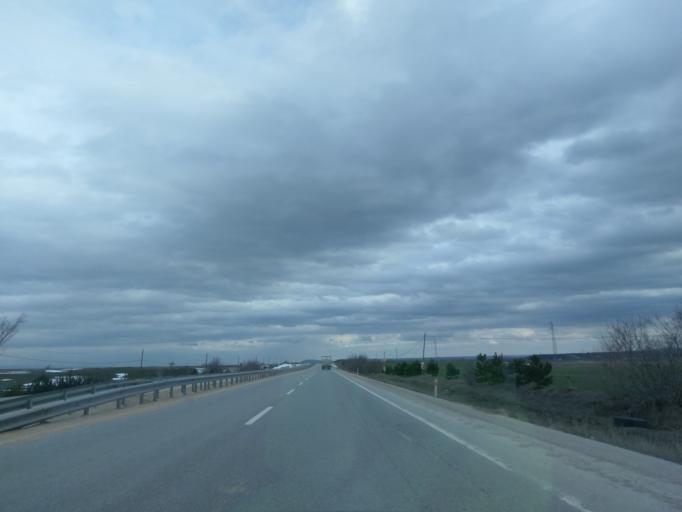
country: TR
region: Eskisehir
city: Inonu
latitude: 39.7238
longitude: 30.2724
